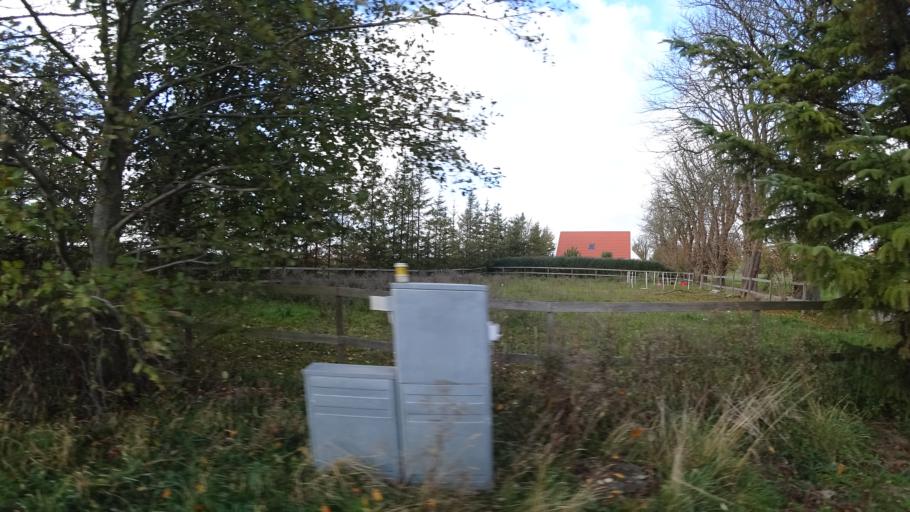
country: SE
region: Skane
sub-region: Staffanstorps Kommun
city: Staffanstorp
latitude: 55.6238
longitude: 13.1982
